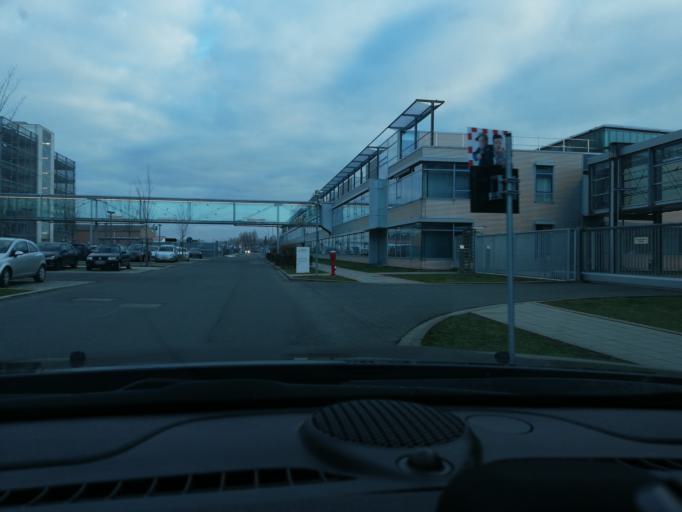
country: DE
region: Bavaria
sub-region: Upper Franconia
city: Forchheim
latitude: 49.7023
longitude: 11.0560
